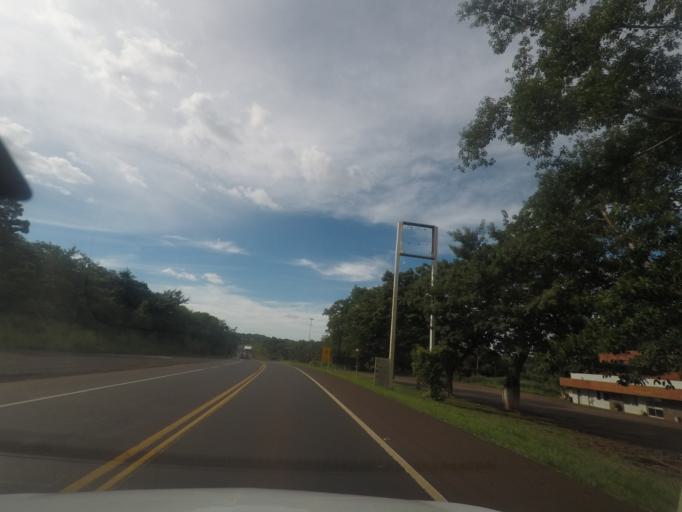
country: BR
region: Minas Gerais
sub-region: Monte Alegre De Minas
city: Monte Alegre de Minas
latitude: -19.0424
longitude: -49.0098
